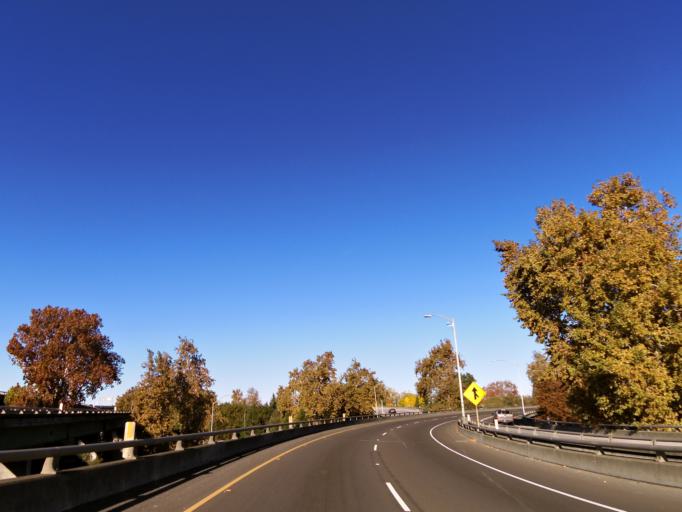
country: US
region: California
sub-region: Sacramento County
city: Sacramento
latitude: 38.5682
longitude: -121.5081
